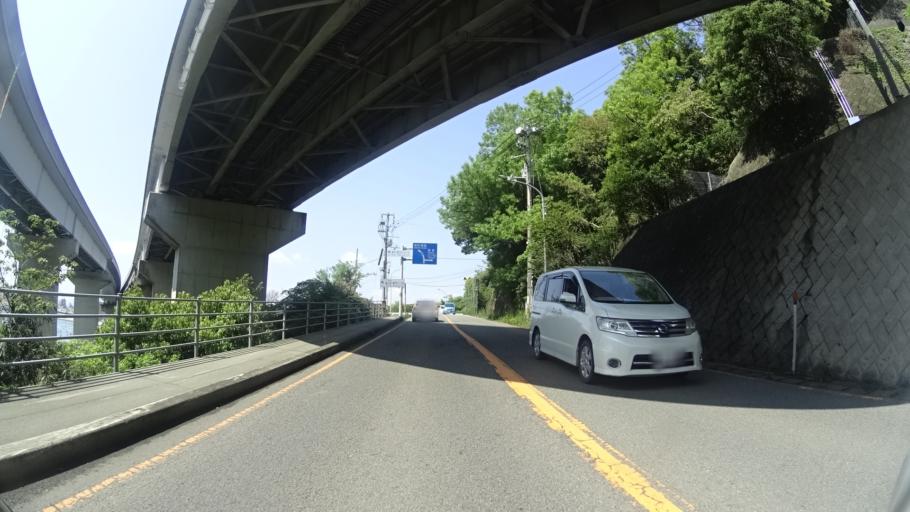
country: JP
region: Tokushima
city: Narutocho-mitsuishi
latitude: 34.1955
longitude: 134.6144
